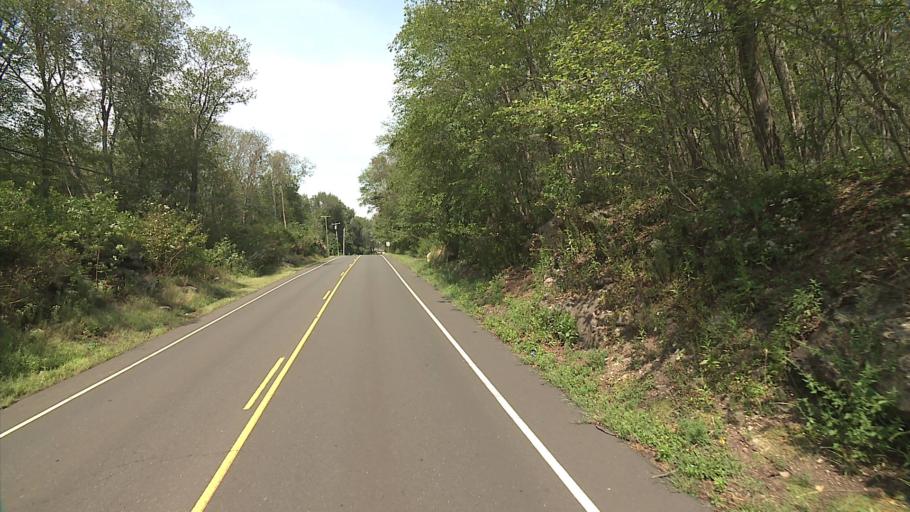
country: US
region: Connecticut
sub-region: Middlesex County
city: Durham
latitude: 41.4426
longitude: -72.6597
